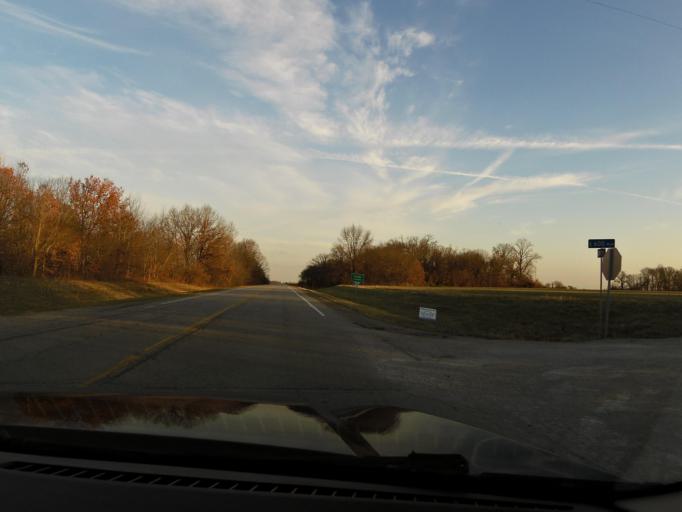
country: US
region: Illinois
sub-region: Fayette County
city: Vandalia
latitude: 38.8234
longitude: -89.0880
